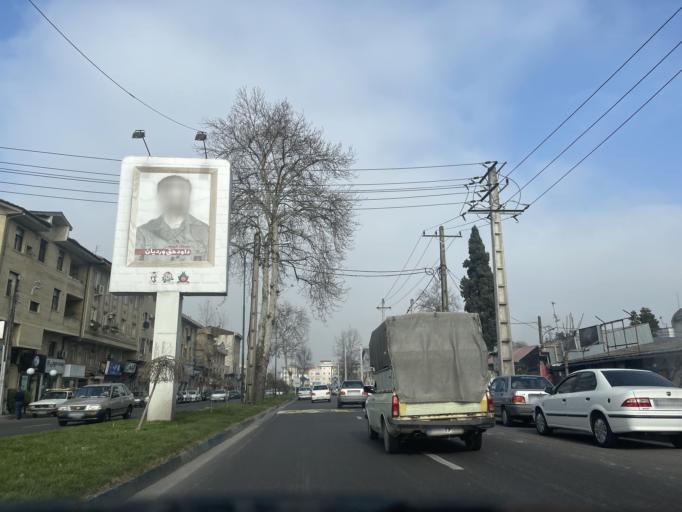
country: IR
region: Gilan
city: Rasht
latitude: 37.2731
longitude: 49.6084
